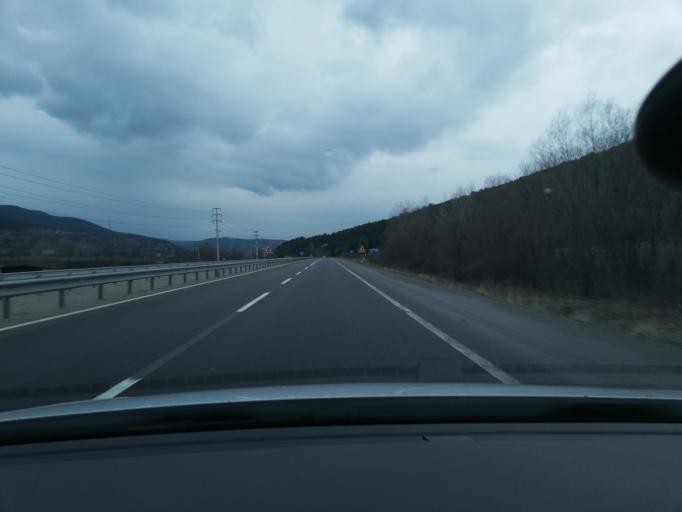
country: TR
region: Bolu
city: Yenicaga
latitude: 40.7450
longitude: 31.8597
